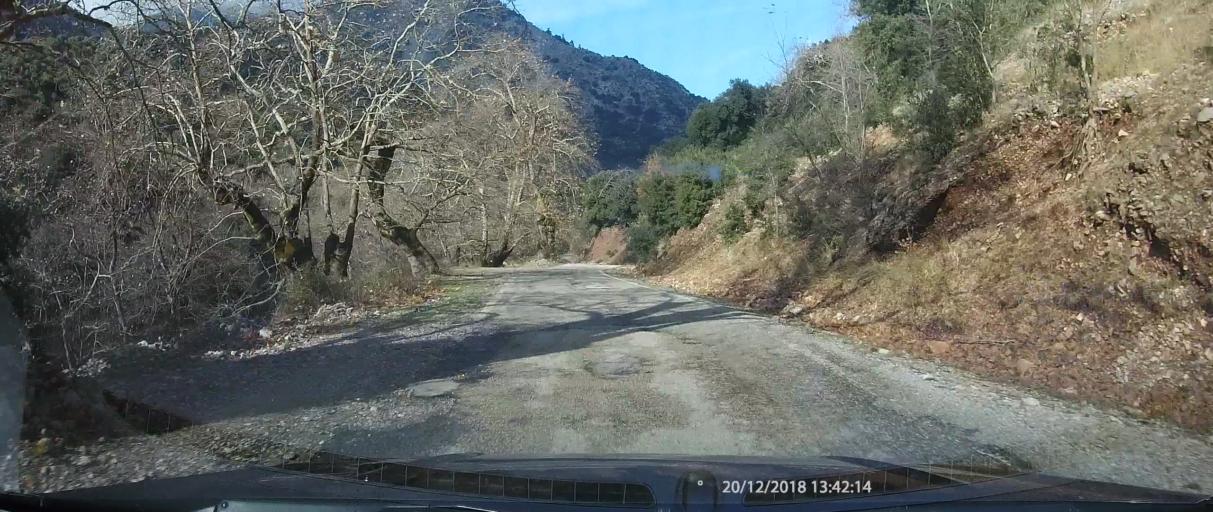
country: GR
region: West Greece
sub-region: Nomos Aitolias kai Akarnanias
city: Thermo
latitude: 38.6519
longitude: 21.6190
